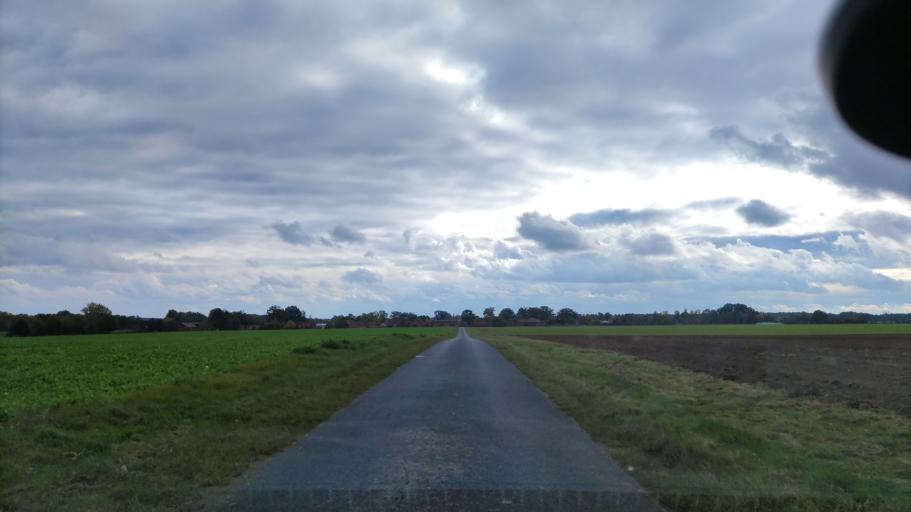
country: DE
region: Lower Saxony
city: Vastorf
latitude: 53.1522
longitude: 10.5349
